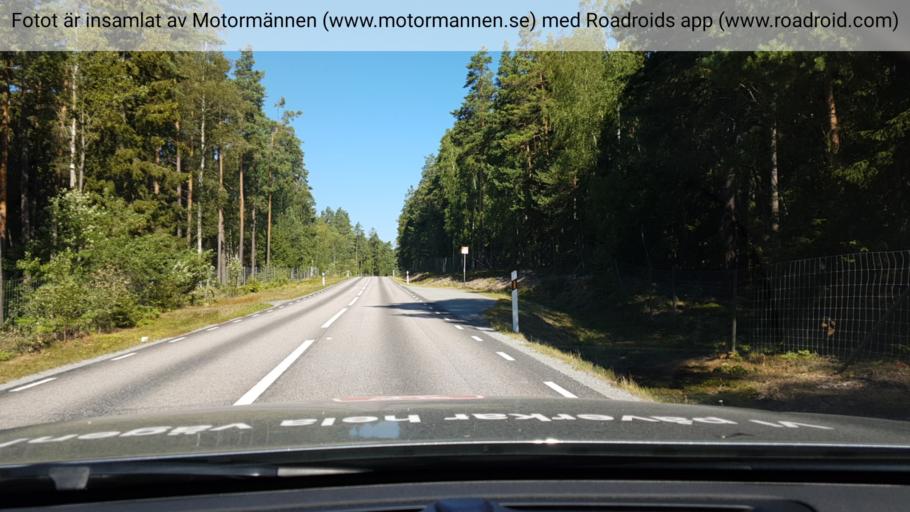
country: SE
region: Stockholm
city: Stenhamra
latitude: 59.3071
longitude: 17.6427
